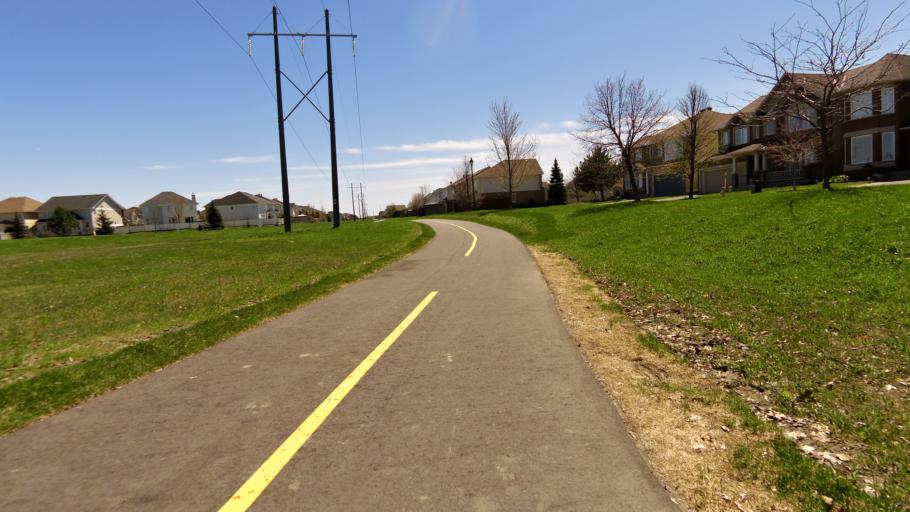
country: CA
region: Ontario
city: Clarence-Rockland
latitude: 45.4571
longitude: -75.4717
